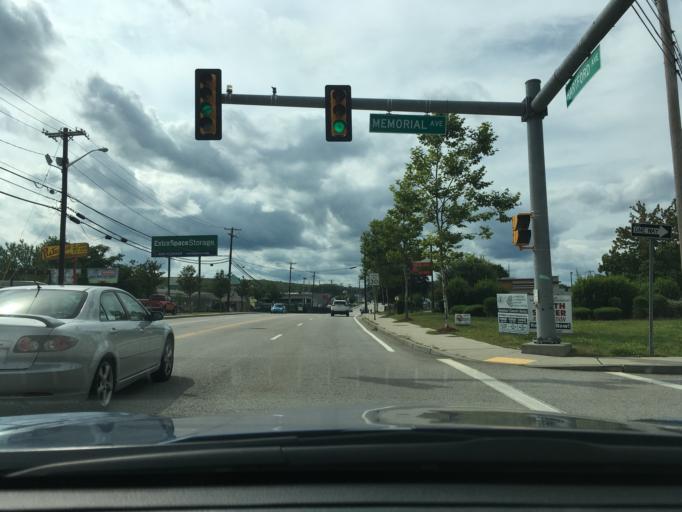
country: US
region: Rhode Island
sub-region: Providence County
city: Johnston
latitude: 41.8258
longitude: -71.5070
